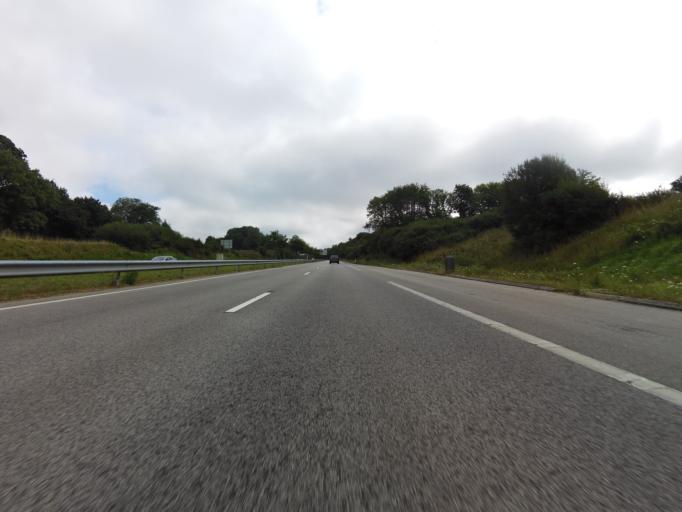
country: FR
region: Brittany
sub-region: Departement du Finistere
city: Quimper
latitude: 48.0169
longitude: -4.1125
